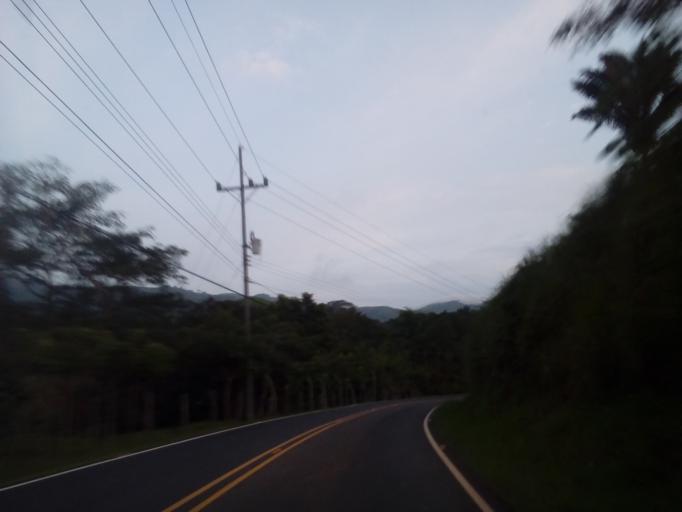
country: CR
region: Guanacaste
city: Hojancha
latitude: 10.0160
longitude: -85.5009
